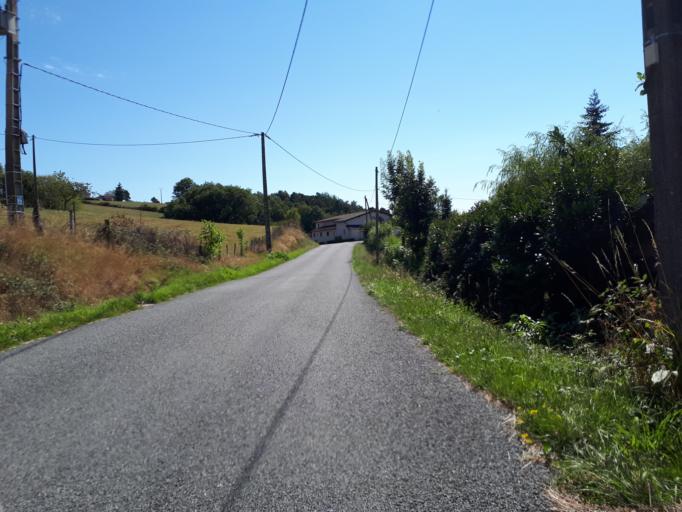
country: FR
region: Rhone-Alpes
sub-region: Departement de la Loire
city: Bussieres
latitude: 45.8315
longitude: 4.2781
